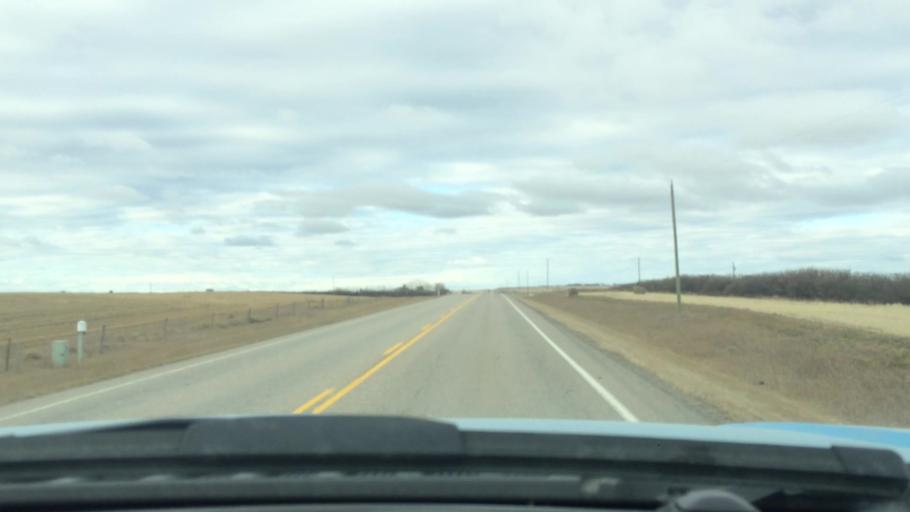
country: CA
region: Alberta
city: Airdrie
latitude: 51.2125
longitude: -114.0654
